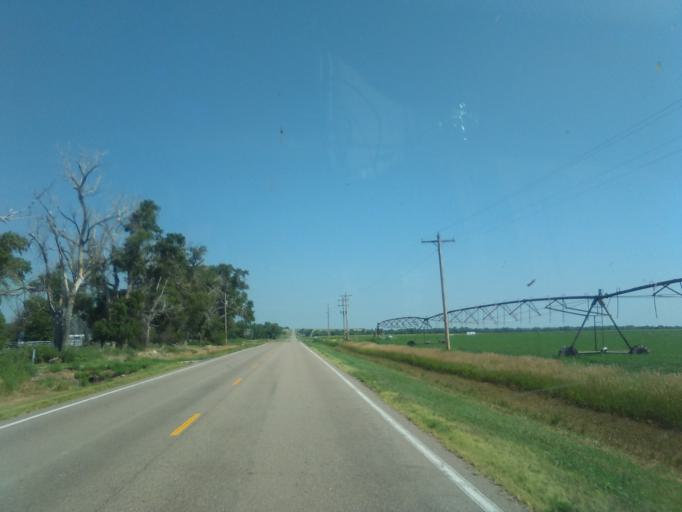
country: US
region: Nebraska
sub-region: Dundy County
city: Benkelman
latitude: 39.9982
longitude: -101.5422
